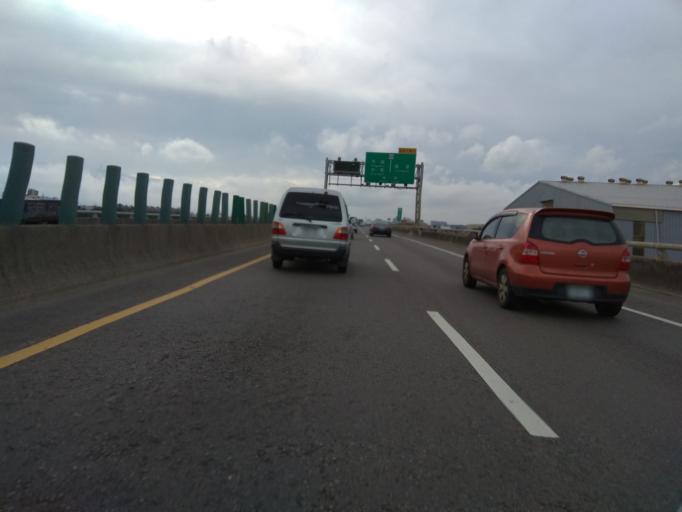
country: TW
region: Taiwan
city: Daxi
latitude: 24.9213
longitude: 121.2225
